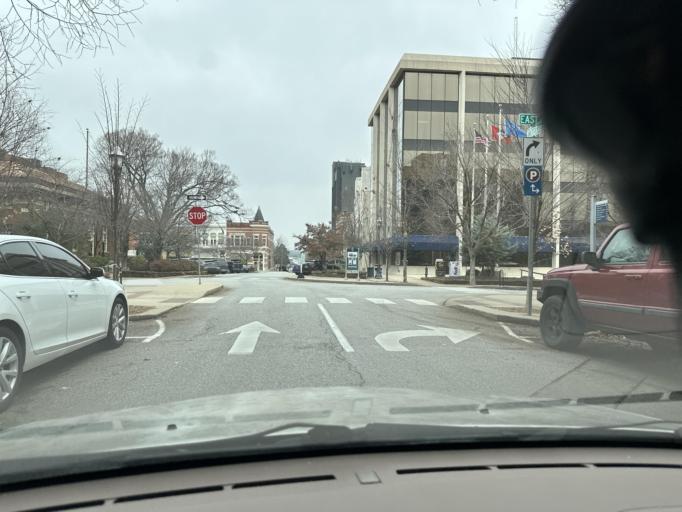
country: US
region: Arkansas
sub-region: Washington County
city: Fayetteville
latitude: 36.0626
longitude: -94.1594
